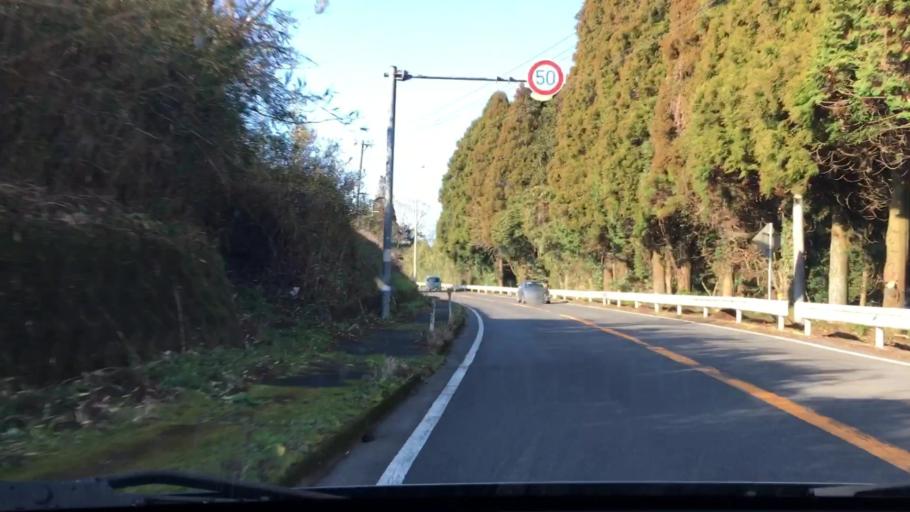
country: JP
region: Kagoshima
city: Sueyoshicho-ninokata
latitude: 31.6783
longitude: 130.9325
